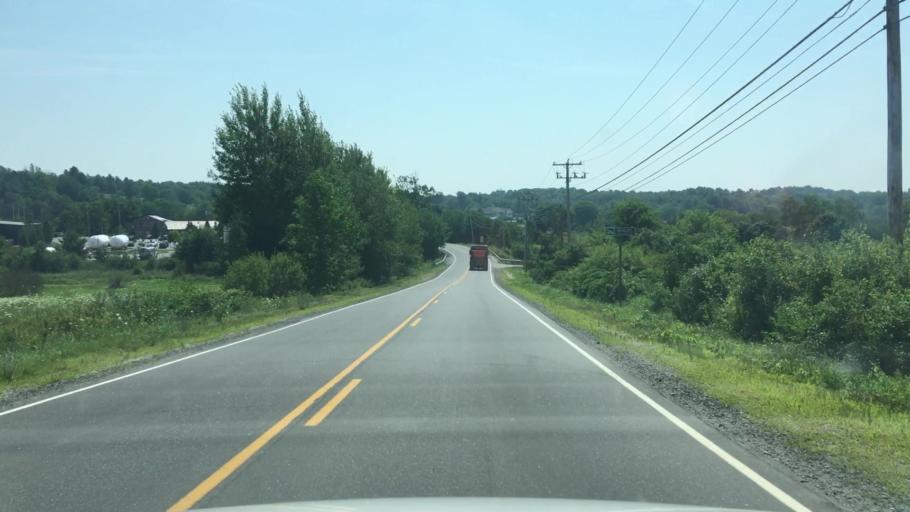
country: US
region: Maine
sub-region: Kennebec County
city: Hallowell
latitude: 44.3000
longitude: -69.8129
